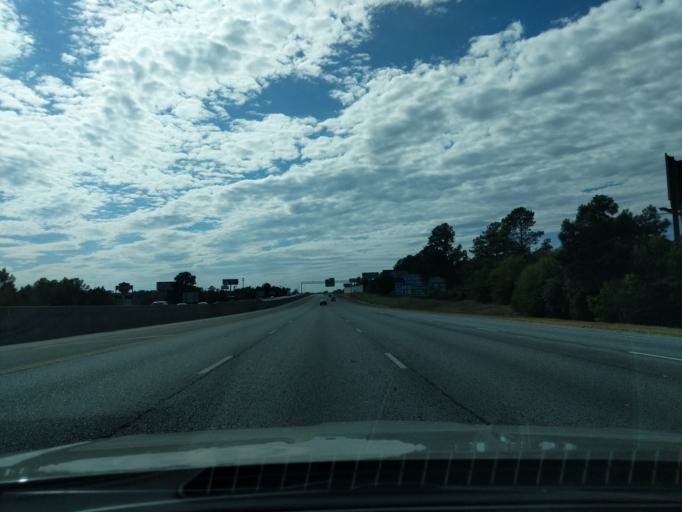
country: US
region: Georgia
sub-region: Columbia County
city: Martinez
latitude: 33.4864
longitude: -82.1146
